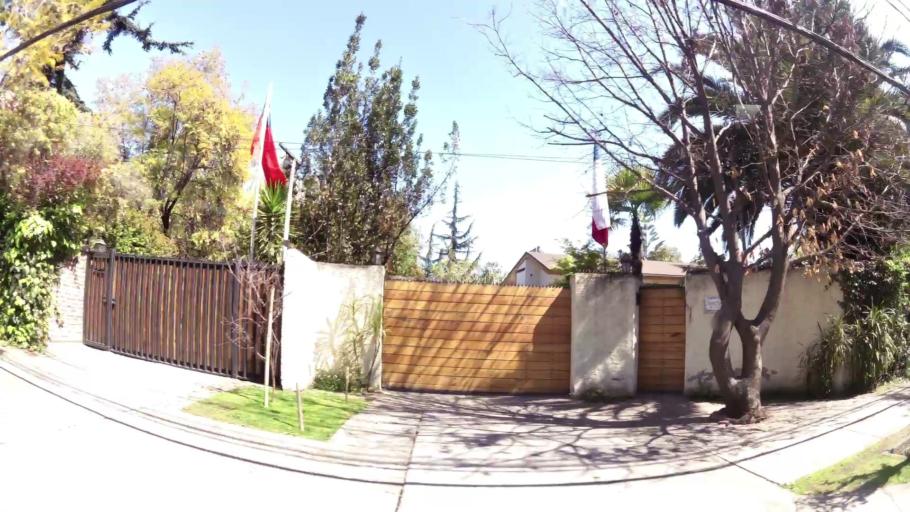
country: CL
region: Santiago Metropolitan
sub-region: Provincia de Santiago
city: Villa Presidente Frei, Nunoa, Santiago, Chile
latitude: -33.4347
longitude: -70.5327
